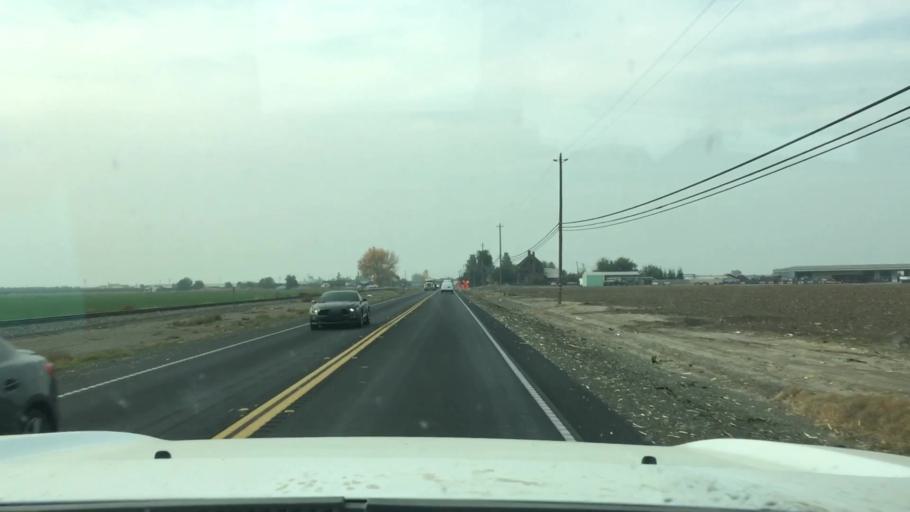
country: US
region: California
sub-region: San Joaquin County
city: Manteca
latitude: 37.8287
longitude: -121.1470
